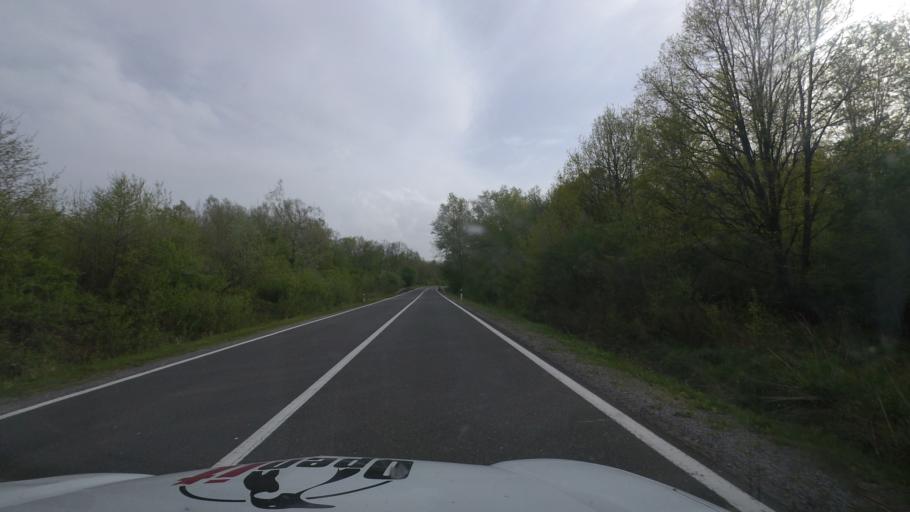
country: HR
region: Sisacko-Moslavacka
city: Gvozd
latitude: 45.3285
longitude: 15.9711
